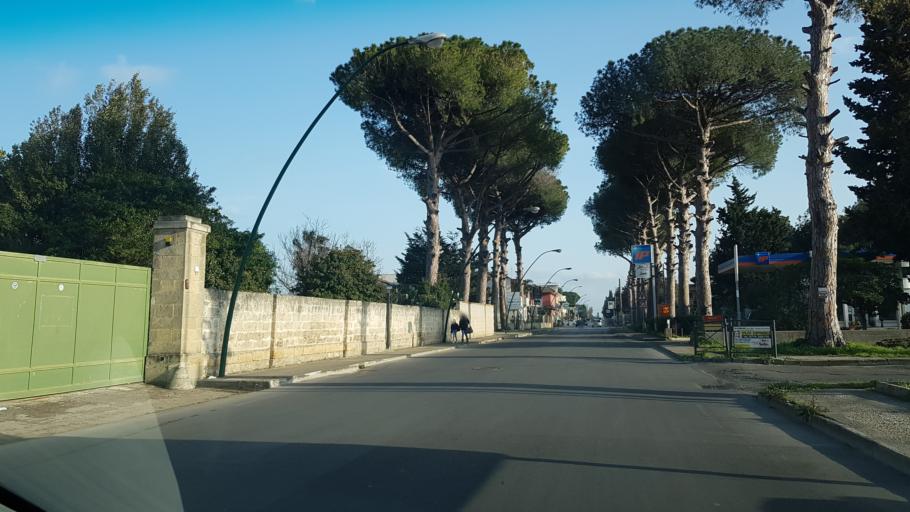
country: IT
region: Apulia
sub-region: Provincia di Lecce
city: Squinzano
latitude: 40.4323
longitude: 18.0493
